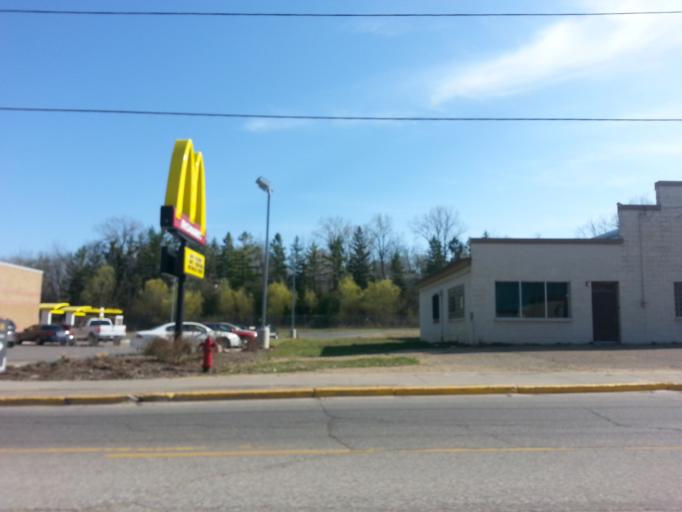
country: US
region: Wisconsin
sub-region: Pierce County
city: Ellsworth
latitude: 44.7321
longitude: -92.4783
